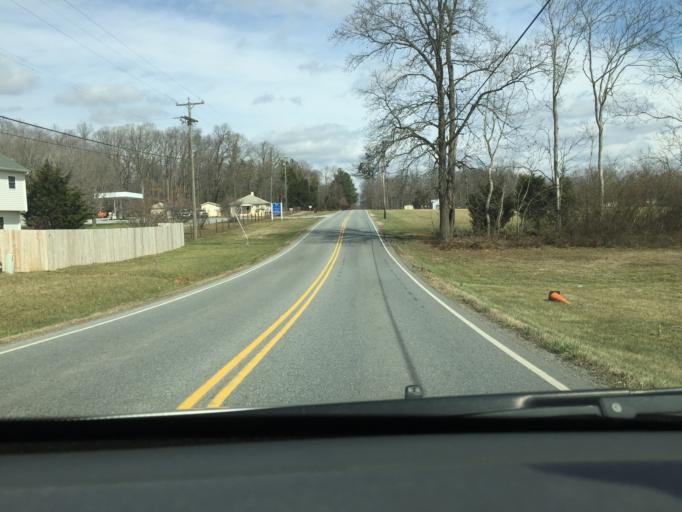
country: US
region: Virginia
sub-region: Bedford County
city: Forest
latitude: 37.3145
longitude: -79.3118
